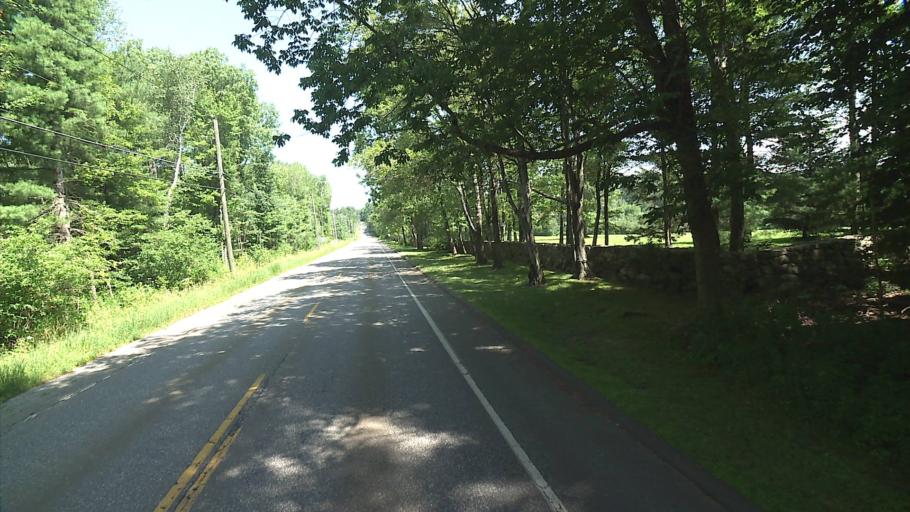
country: US
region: Connecticut
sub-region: Litchfield County
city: New Preston
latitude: 41.7586
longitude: -73.3531
